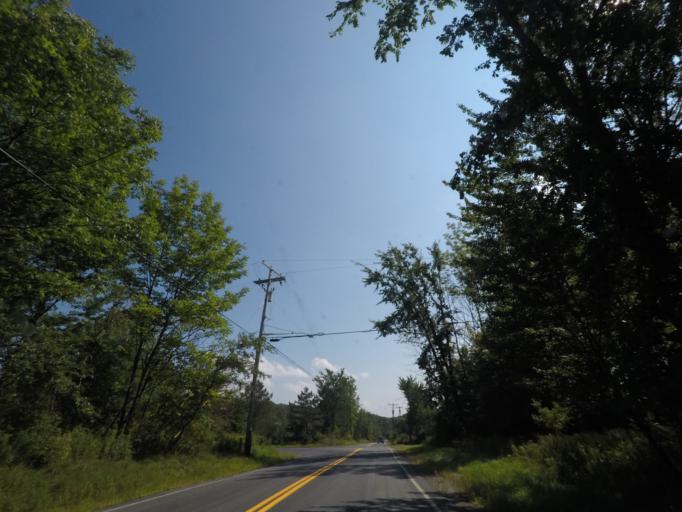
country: US
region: New York
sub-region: Rensselaer County
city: Poestenkill
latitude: 42.7336
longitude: -73.5097
